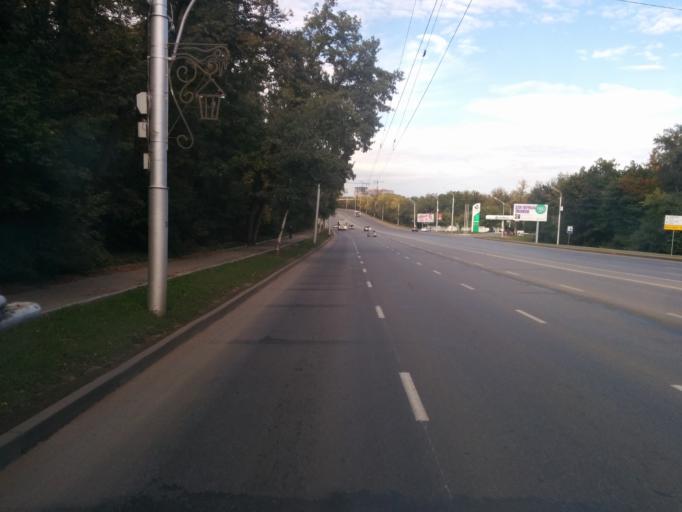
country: RU
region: Bashkortostan
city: Ufa
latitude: 54.8027
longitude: 56.0457
